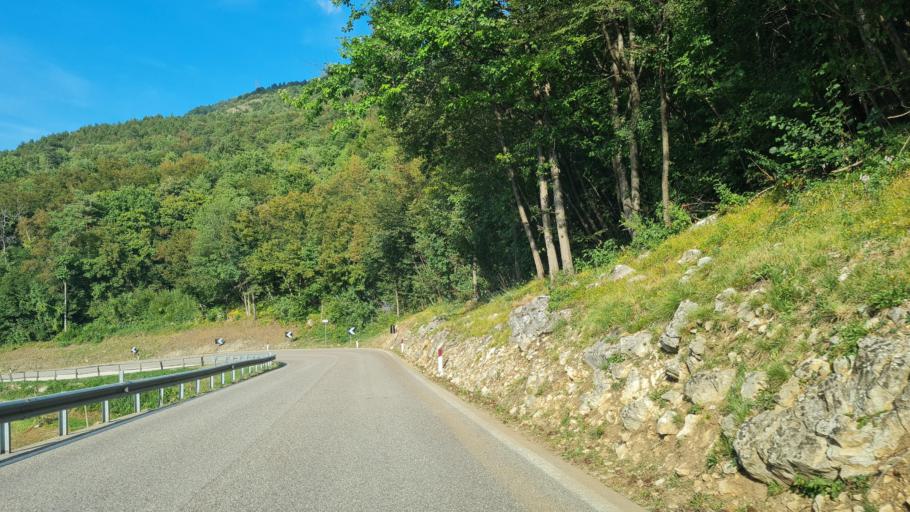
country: IT
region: Trentino-Alto Adige
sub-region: Provincia di Trento
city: Mattarello
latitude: 46.0245
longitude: 11.1459
